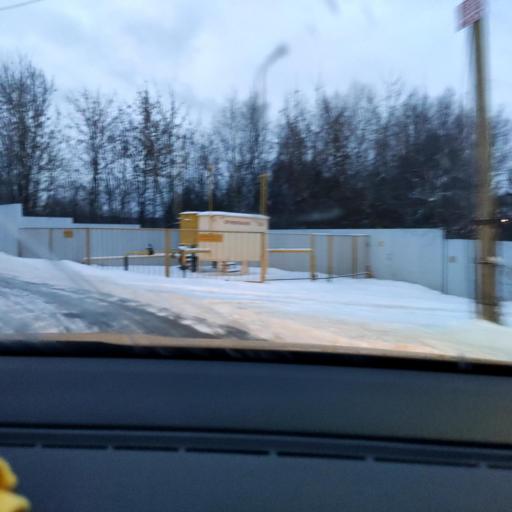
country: RU
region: Moskovskaya
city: Skolkovo
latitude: 55.6859
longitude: 37.3651
